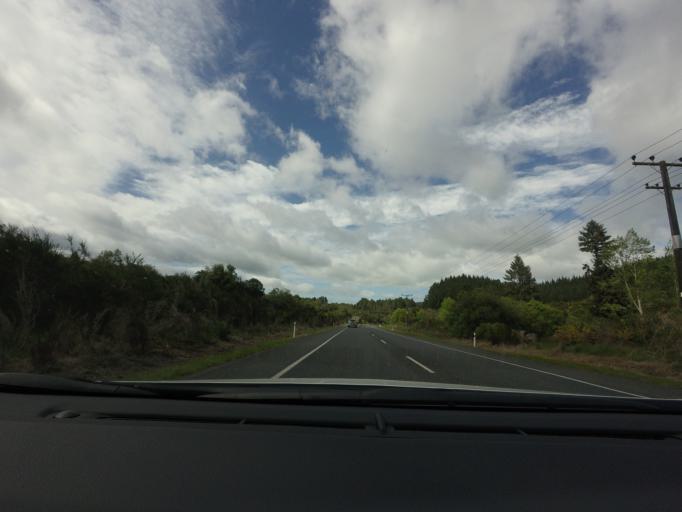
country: NZ
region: Bay of Plenty
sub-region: Rotorua District
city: Rotorua
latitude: -38.3188
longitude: 176.3742
